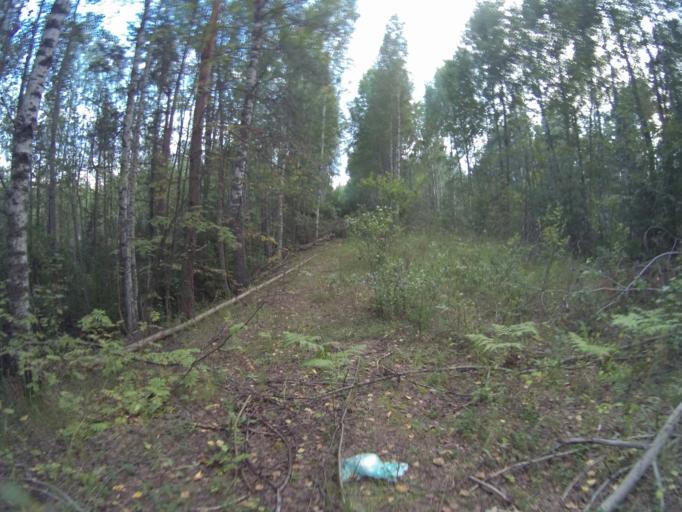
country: RU
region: Vladimir
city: Raduzhnyy
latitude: 55.9773
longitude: 40.2620
